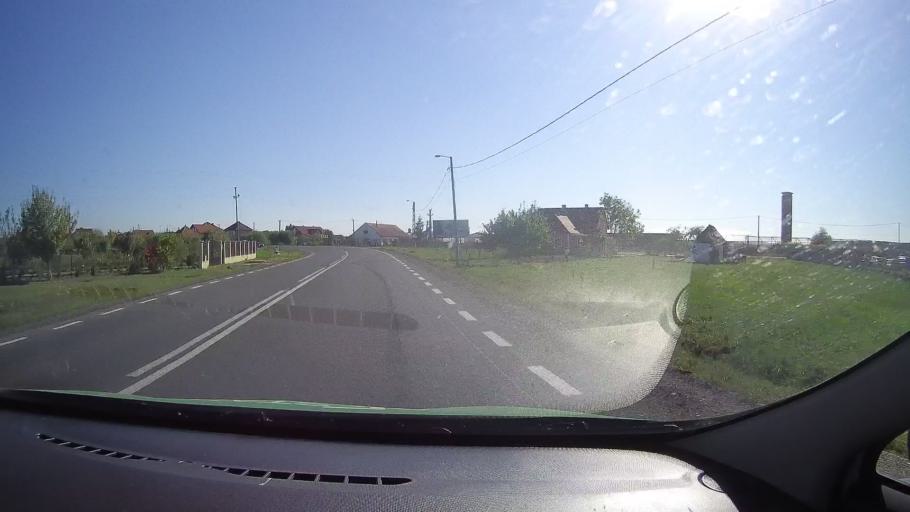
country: RO
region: Satu Mare
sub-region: Oras Ardud
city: Ardud
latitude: 47.6543
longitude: 22.8857
